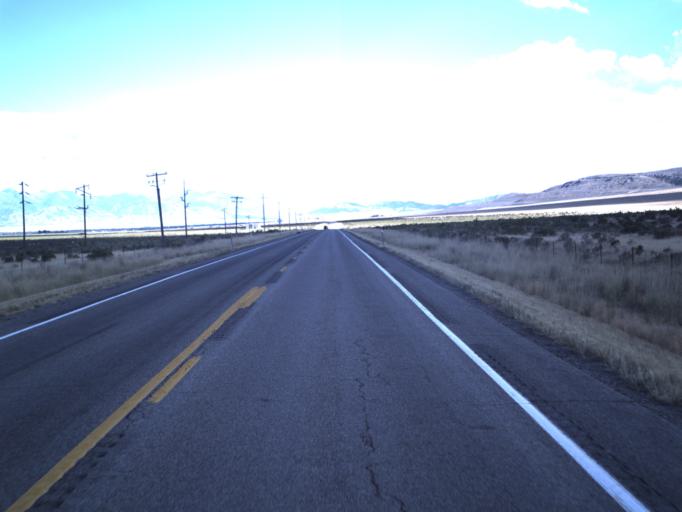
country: US
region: Utah
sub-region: Tooele County
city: Grantsville
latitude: 40.6725
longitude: -112.5482
